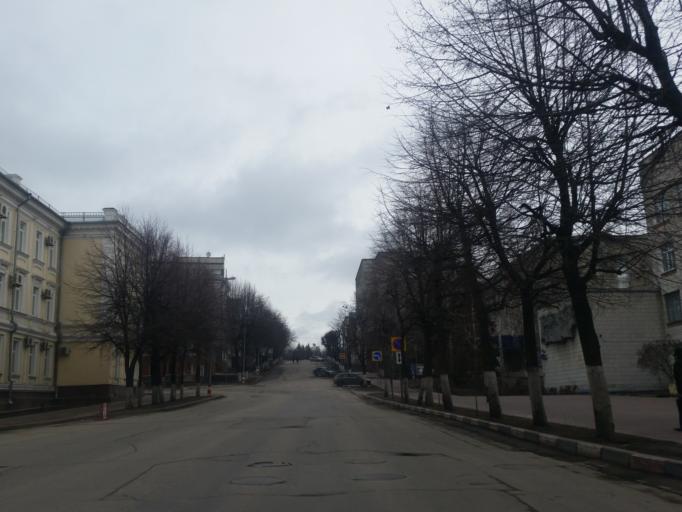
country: RU
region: Ulyanovsk
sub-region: Ulyanovskiy Rayon
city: Ulyanovsk
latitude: 54.3119
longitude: 48.4006
